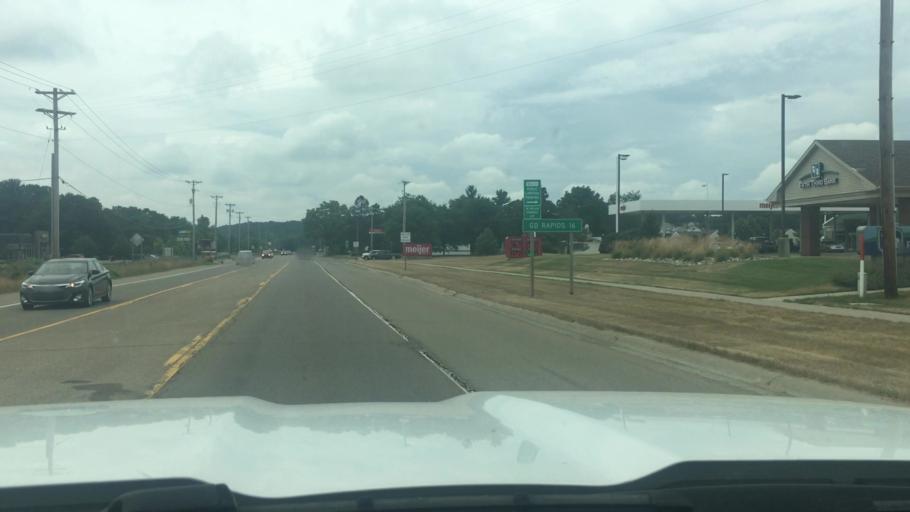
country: US
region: Michigan
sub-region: Kent County
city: Lowell
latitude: 42.9307
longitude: -85.3738
